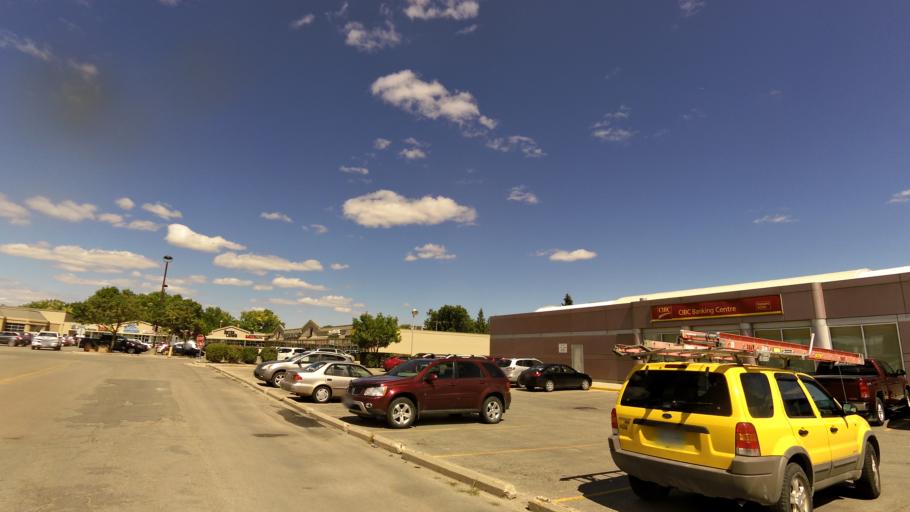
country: CA
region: Manitoba
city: Headingley
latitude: 49.8829
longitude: -97.2988
